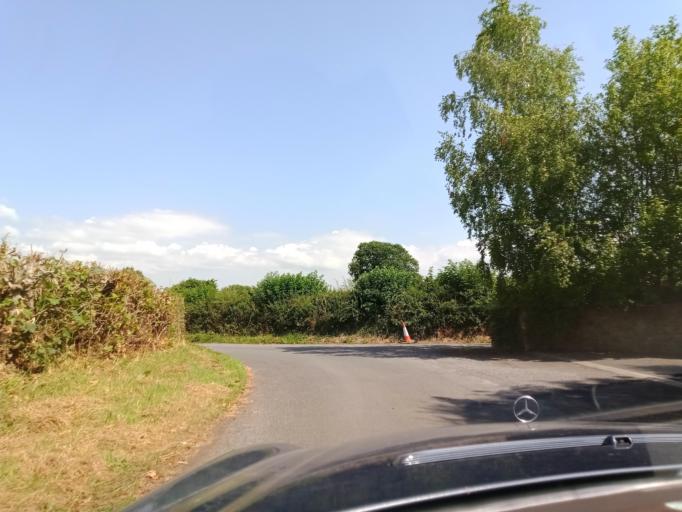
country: IE
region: Leinster
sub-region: Kilkenny
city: Mooncoin
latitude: 52.3104
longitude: -7.2722
